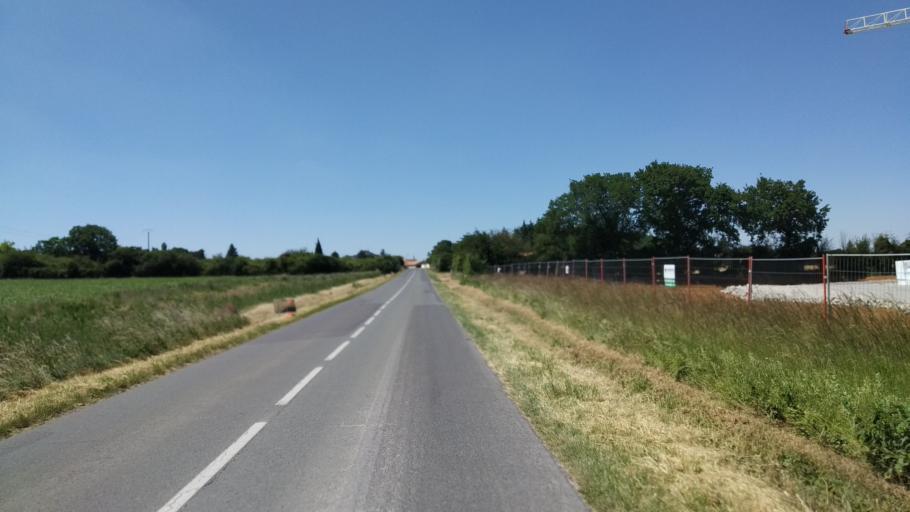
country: FR
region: Poitou-Charentes
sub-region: Departement de la Vienne
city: Biard
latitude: 46.6004
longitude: 0.2905
